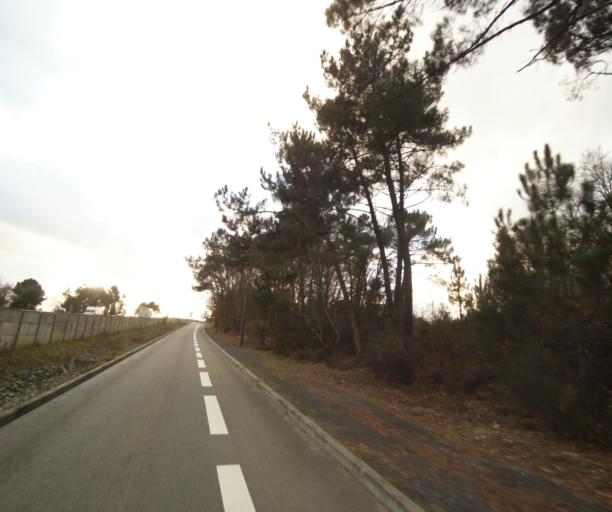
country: FR
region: Pays de la Loire
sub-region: Departement de la Sarthe
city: Le Mans
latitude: 47.9645
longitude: 0.2268
